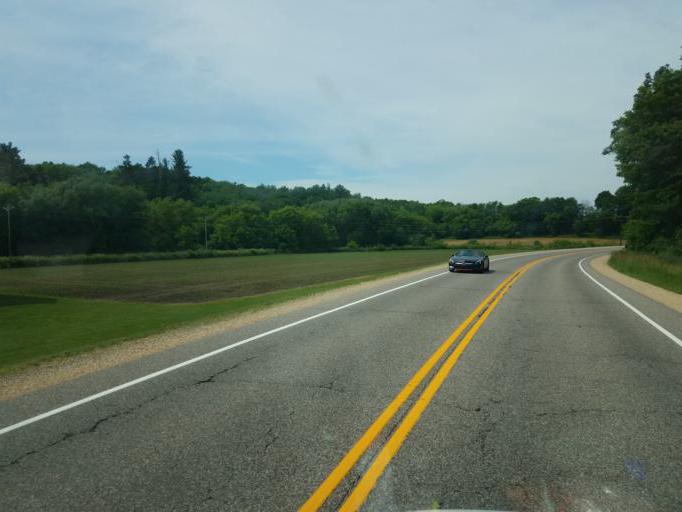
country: US
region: Wisconsin
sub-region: Juneau County
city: Elroy
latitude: 43.7676
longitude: -90.2317
